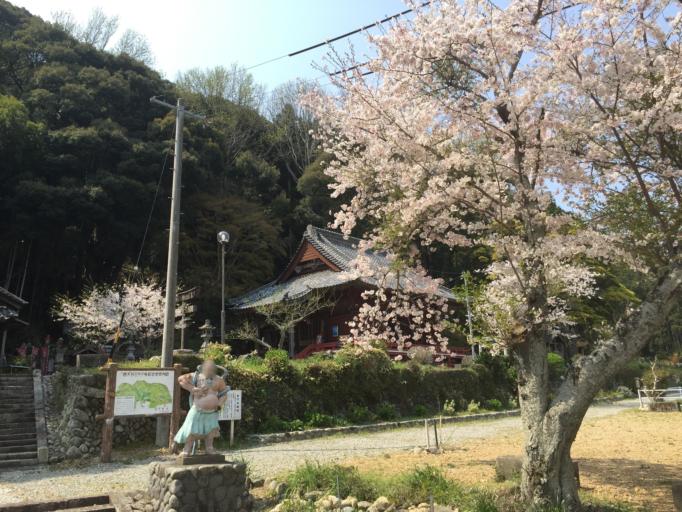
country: JP
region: Shizuoka
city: Kakegawa
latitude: 34.6925
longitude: 137.9861
